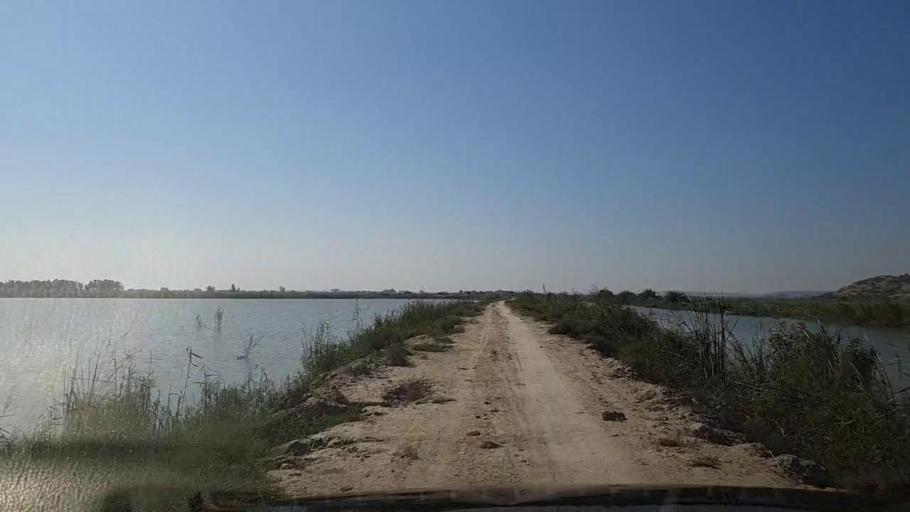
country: PK
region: Sindh
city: Thatta
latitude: 24.6769
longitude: 67.8895
